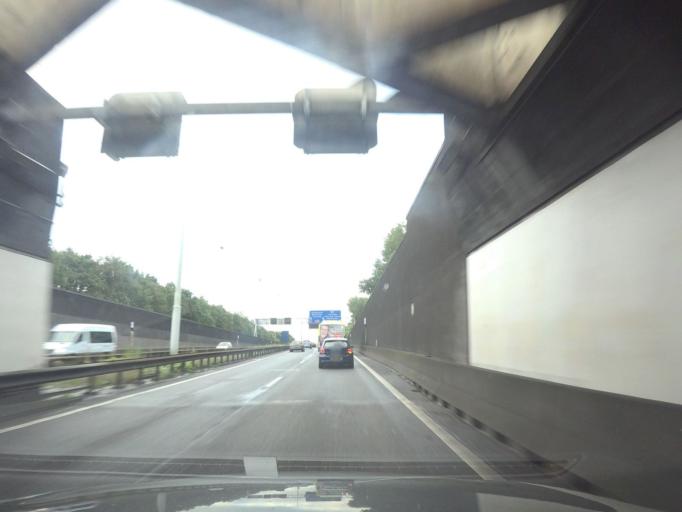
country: NL
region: North Holland
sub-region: Gemeente Velsen
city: Velsen-Zuid
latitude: 52.4607
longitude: 4.6543
